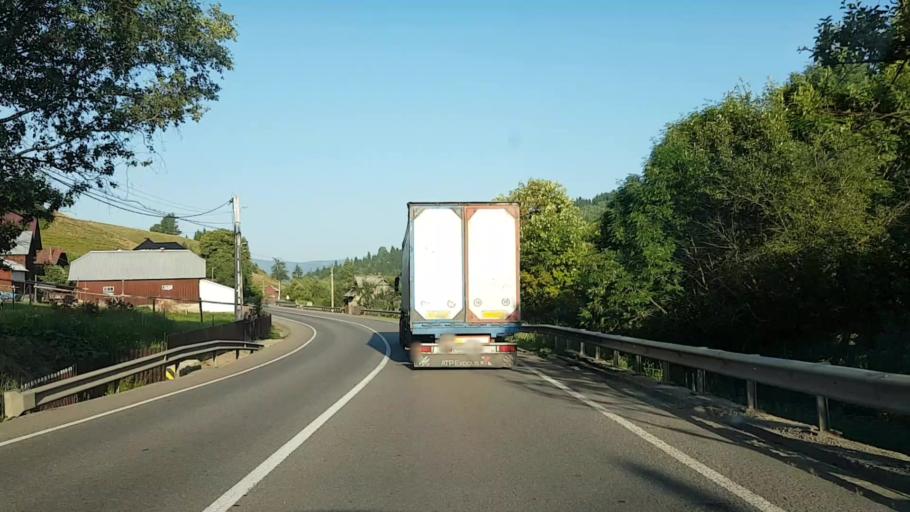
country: RO
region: Suceava
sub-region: Comuna Dorna Candrenilor
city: Dorna Candrenilor
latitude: 47.3571
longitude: 25.2762
